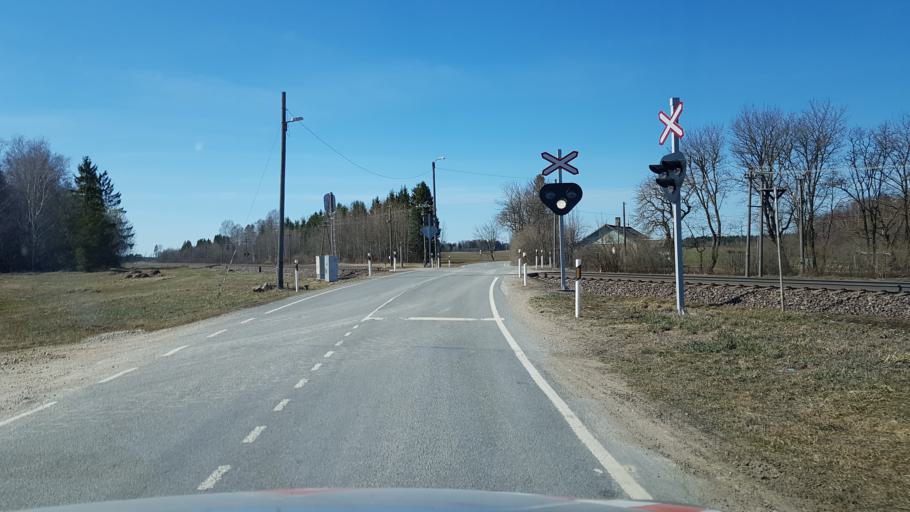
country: EE
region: Laeaene-Virumaa
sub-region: Someru vald
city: Someru
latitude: 59.3496
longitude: 26.4871
